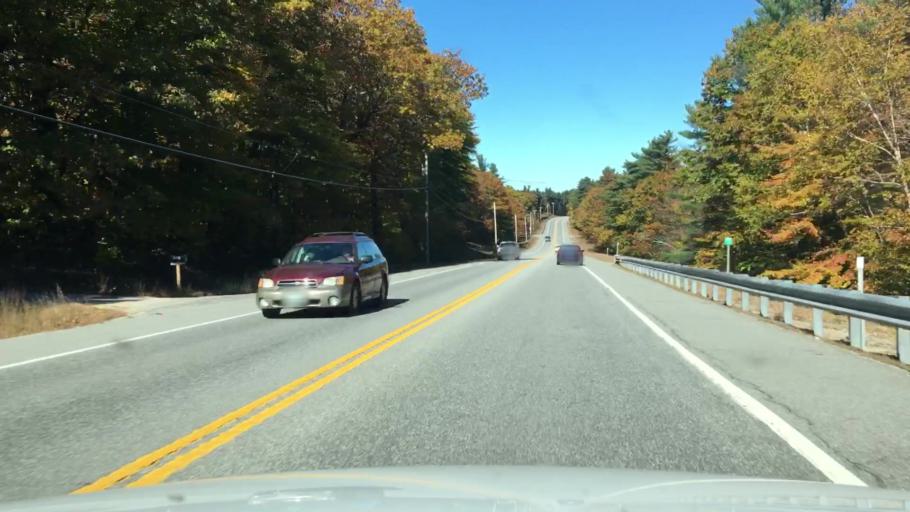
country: US
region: New Hampshire
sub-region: Carroll County
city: Wakefield
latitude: 43.6002
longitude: -71.0335
